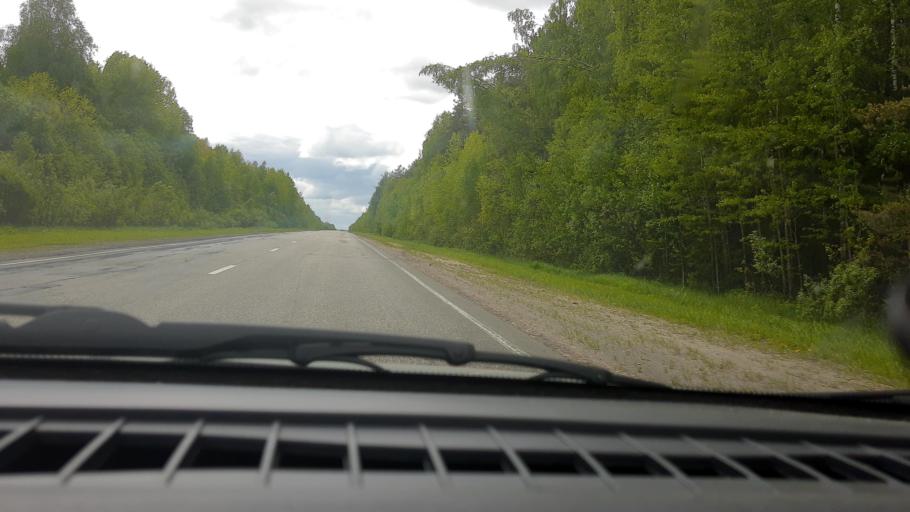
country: RU
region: Nizjnij Novgorod
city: Vladimirskoye
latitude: 56.9335
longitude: 45.0713
